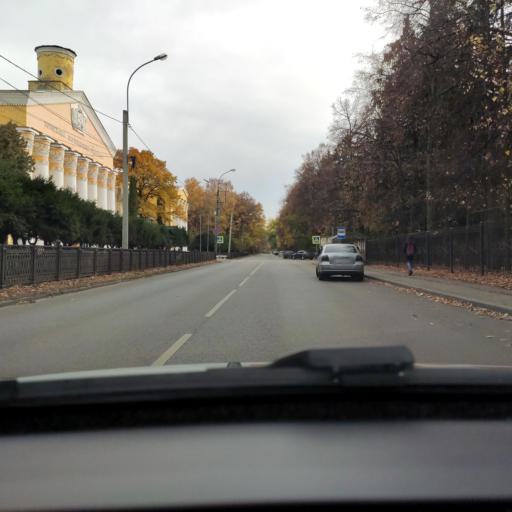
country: RU
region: Voronezj
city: Voronezh
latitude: 51.7193
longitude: 39.2200
